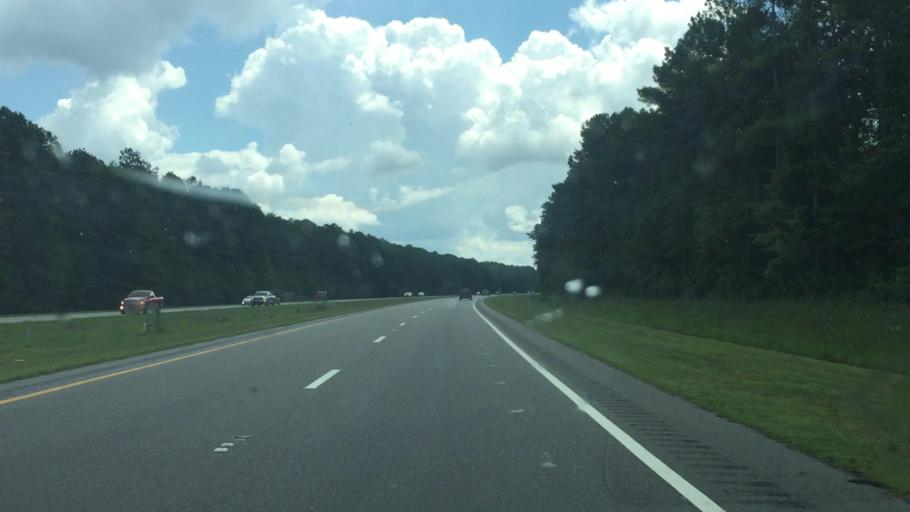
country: US
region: North Carolina
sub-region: Columbus County
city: Chadbourn
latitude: 34.3794
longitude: -78.8528
